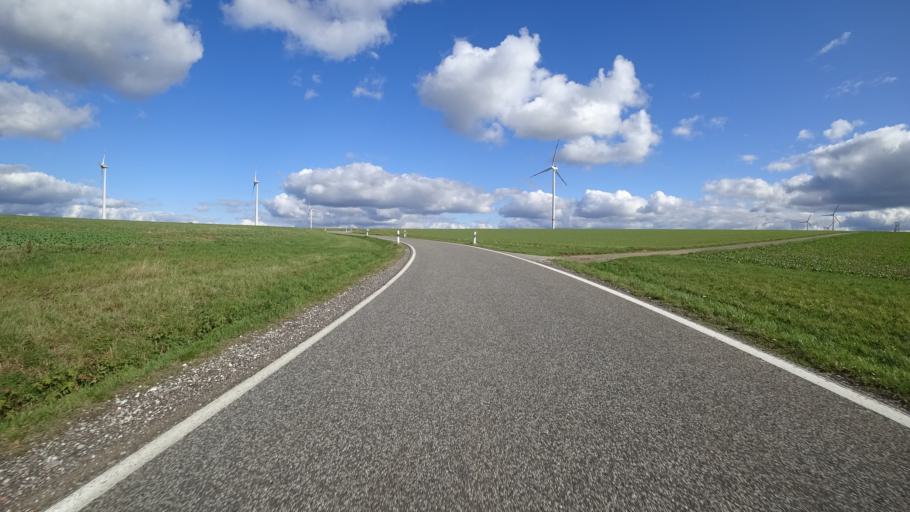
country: DE
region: Rheinland-Pfalz
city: Wuschheim
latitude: 50.0131
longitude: 7.4293
